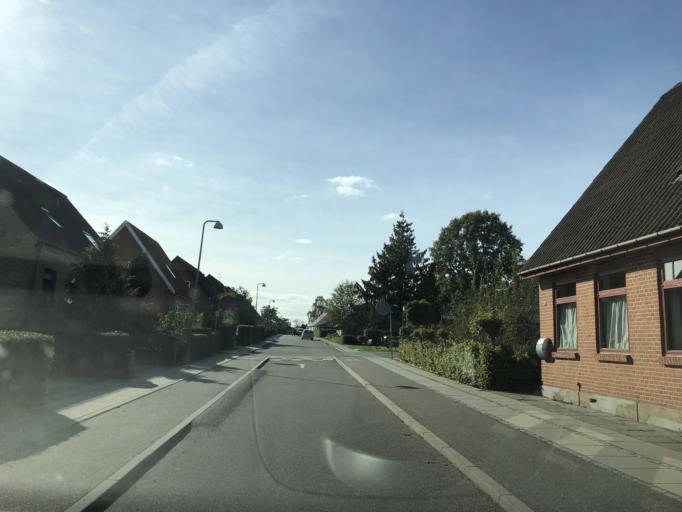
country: DK
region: Central Jutland
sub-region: Syddjurs Kommune
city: Hornslet
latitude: 56.3137
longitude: 10.3138
